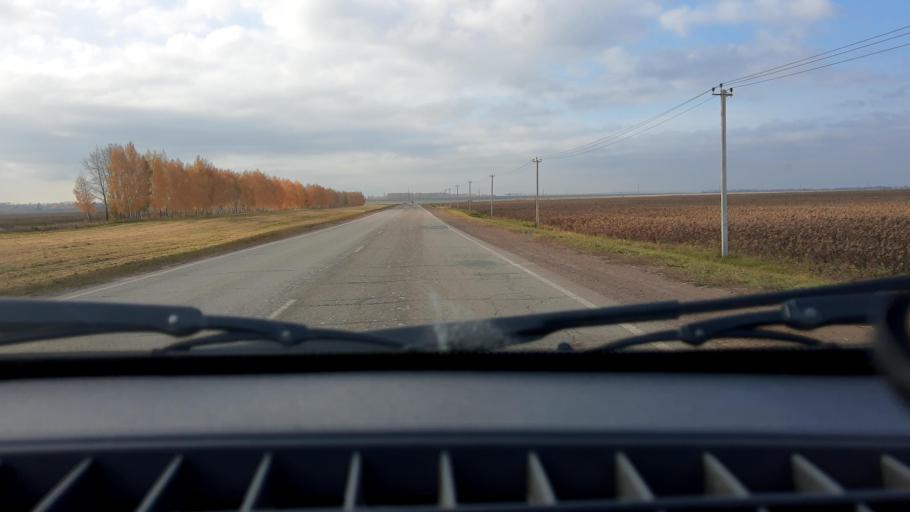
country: RU
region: Bashkortostan
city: Kabakovo
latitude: 54.5450
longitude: 56.0822
